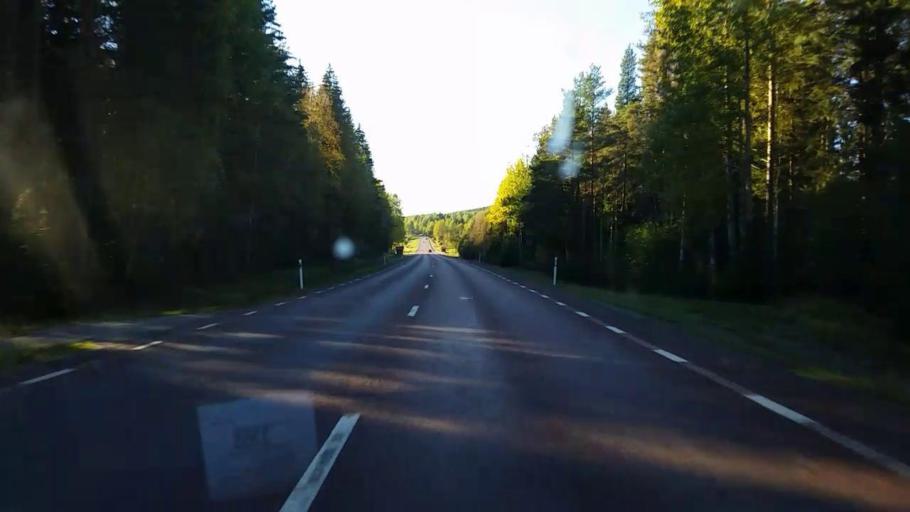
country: SE
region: Gaevleborg
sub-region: Ljusdals Kommun
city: Jaervsoe
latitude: 61.8145
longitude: 16.2002
